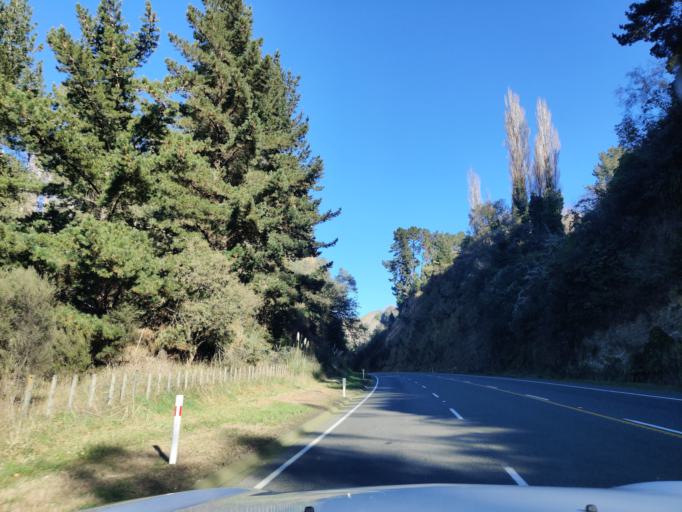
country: NZ
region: Manawatu-Wanganui
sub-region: Ruapehu District
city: Waiouru
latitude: -39.7584
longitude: 175.8103
